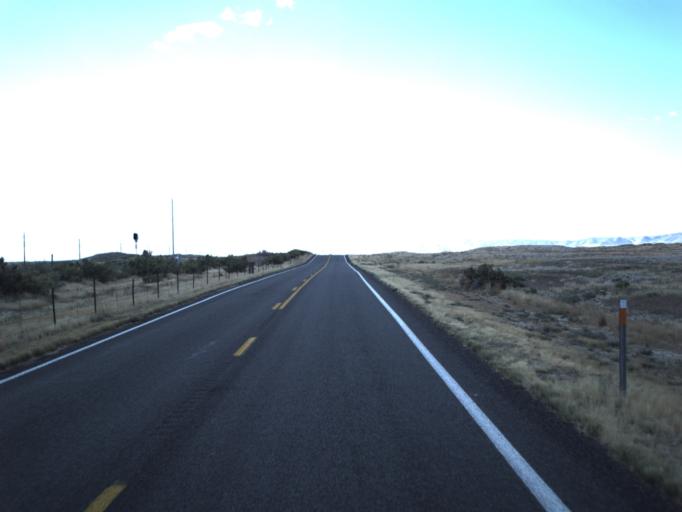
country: US
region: Utah
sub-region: Millard County
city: Delta
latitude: 38.9908
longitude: -112.7912
